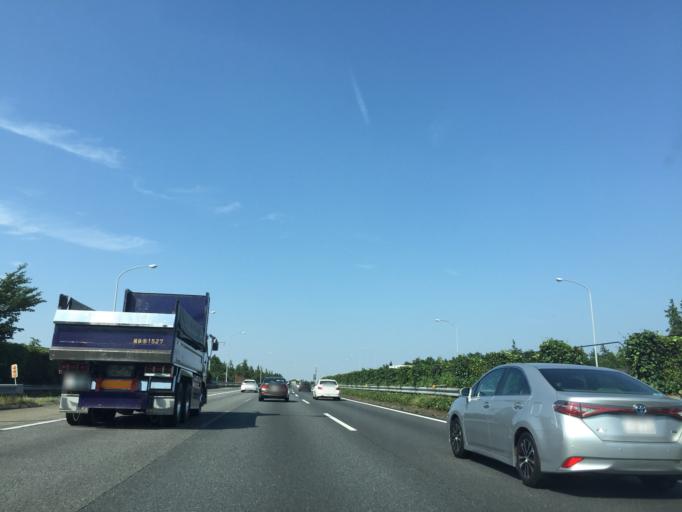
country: JP
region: Kanagawa
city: Minami-rinkan
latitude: 35.4797
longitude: 139.4543
